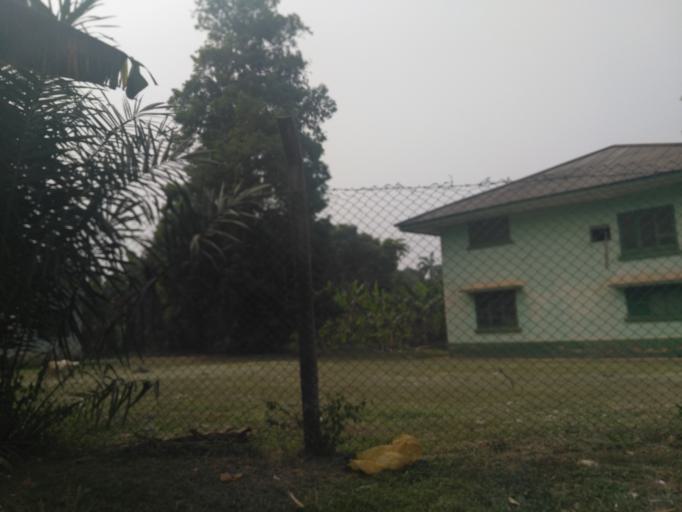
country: GH
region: Ashanti
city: Kumasi
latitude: 6.6775
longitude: -1.6201
